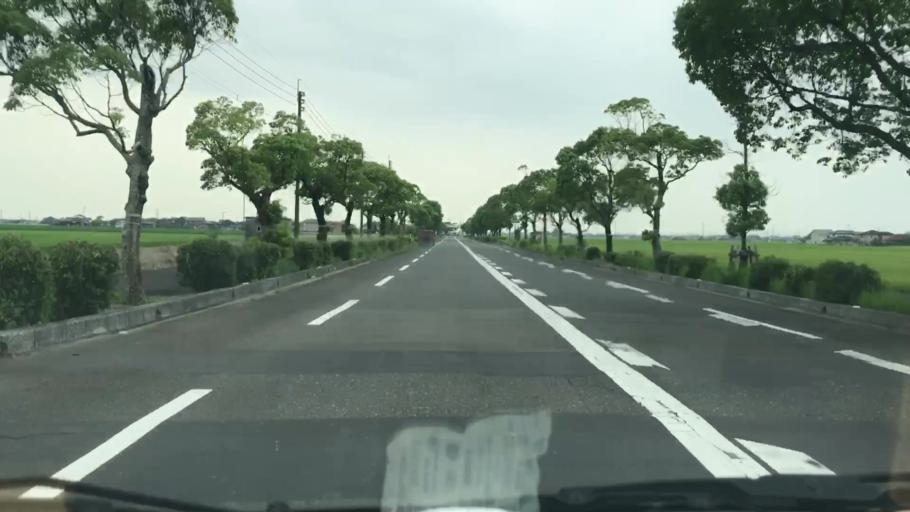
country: JP
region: Saga Prefecture
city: Saga-shi
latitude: 33.2121
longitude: 130.3045
